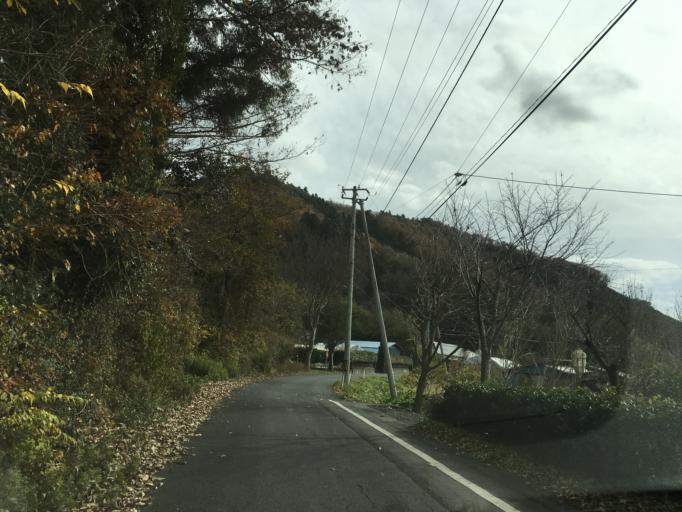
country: JP
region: Iwate
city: Ichinoseki
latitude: 38.7819
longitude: 141.2668
